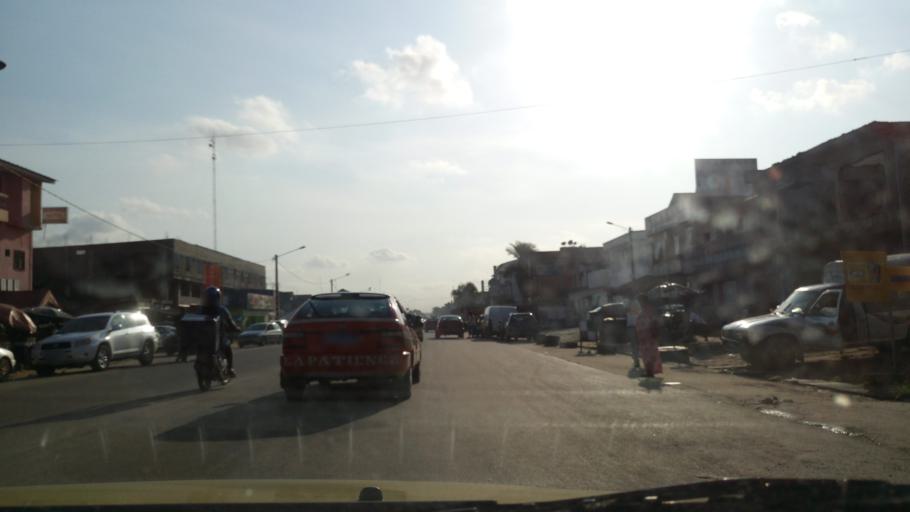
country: CI
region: Lagunes
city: Abobo
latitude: 5.4030
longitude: -3.9789
